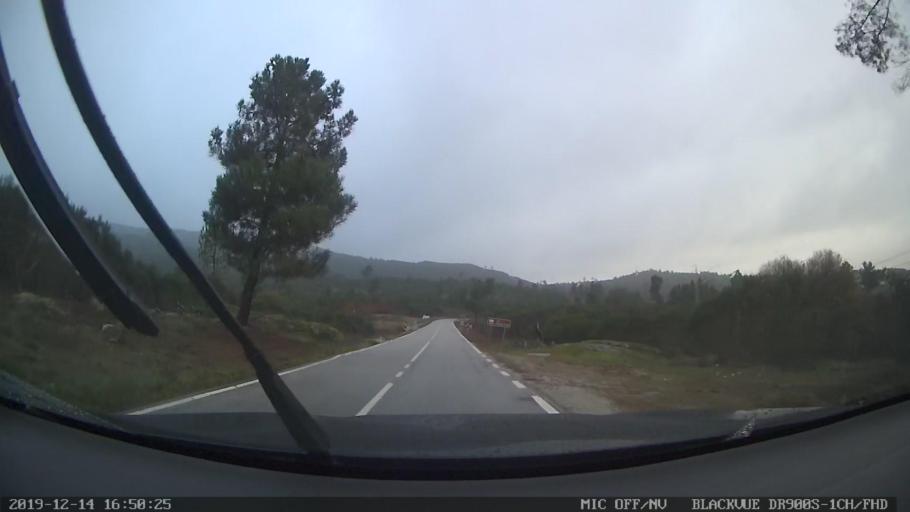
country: PT
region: Vila Real
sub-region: Murca
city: Murca
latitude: 41.4163
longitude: -7.5044
